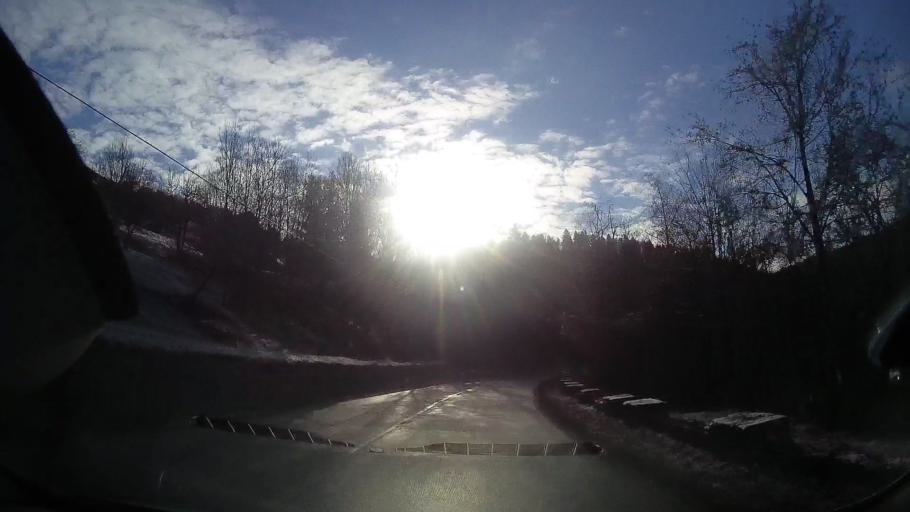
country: RO
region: Alba
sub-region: Comuna Sohodol
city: Sohodol
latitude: 46.3668
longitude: 23.0291
